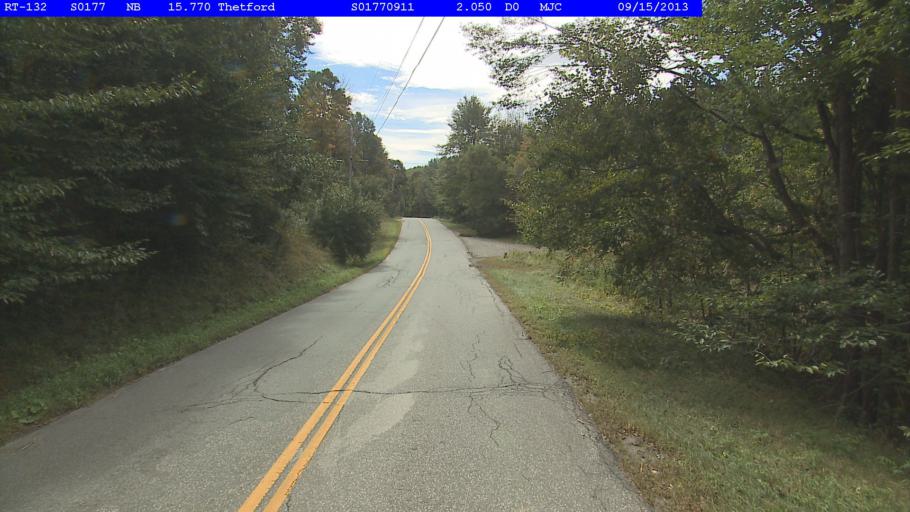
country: US
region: New Hampshire
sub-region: Grafton County
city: Hanover
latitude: 43.8257
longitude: -72.2860
